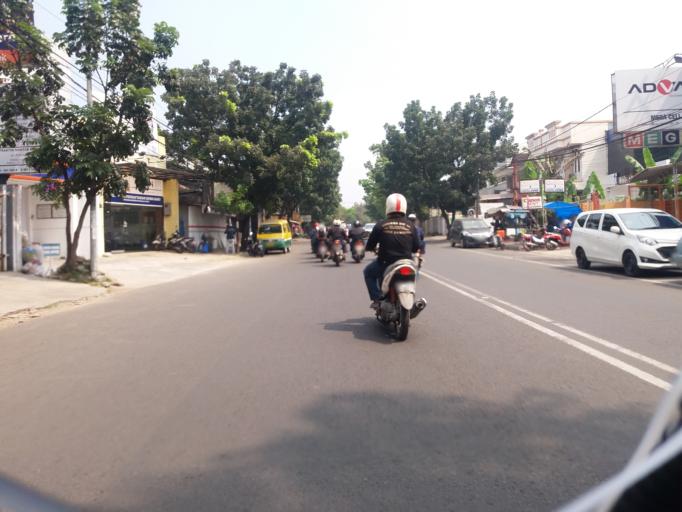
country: ID
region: West Java
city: Bandung
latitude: -6.9075
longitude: 107.5842
